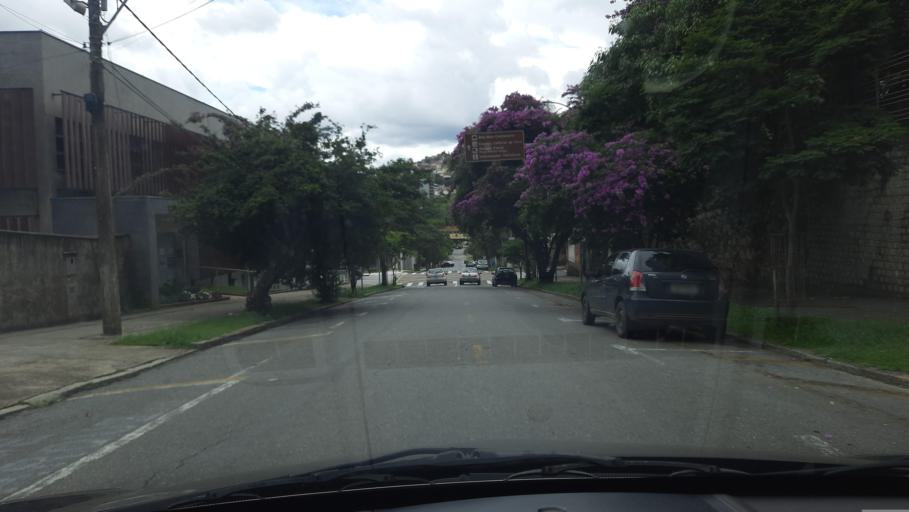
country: BR
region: Minas Gerais
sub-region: Pocos De Caldas
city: Pocos de Caldas
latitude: -21.7831
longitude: -46.5715
